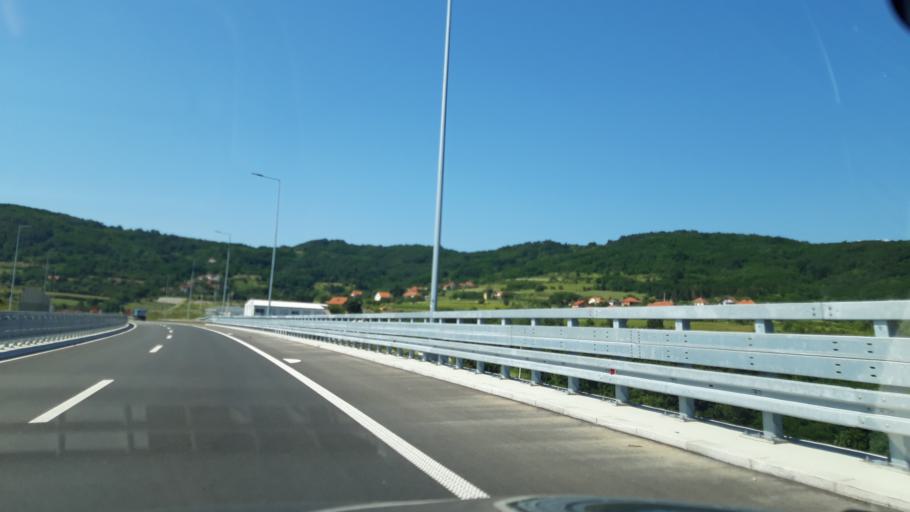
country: RS
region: Central Serbia
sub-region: Pcinjski Okrug
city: Vladicin Han
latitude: 42.7231
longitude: 22.0763
